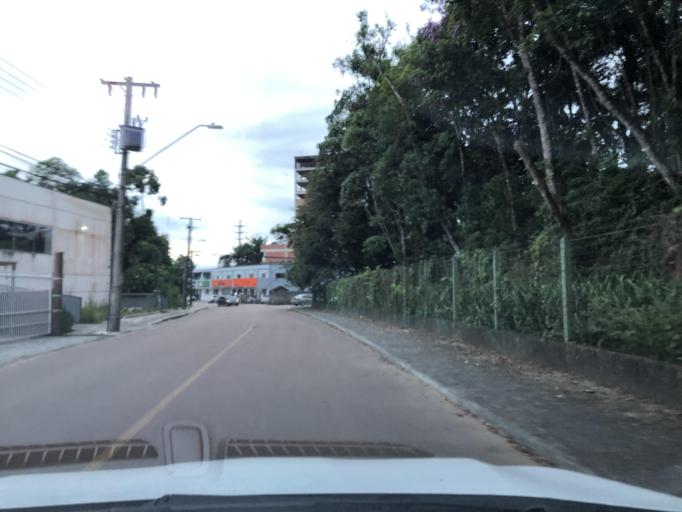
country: BR
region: Santa Catarina
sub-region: Joinville
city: Joinville
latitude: -26.2936
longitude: -48.8788
